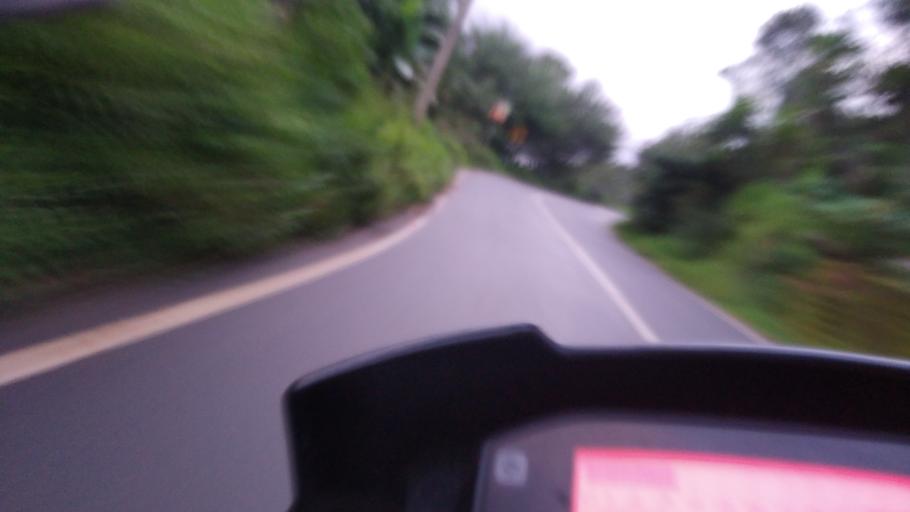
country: IN
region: Kerala
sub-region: Idukki
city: Munnar
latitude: 9.9662
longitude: 77.1078
